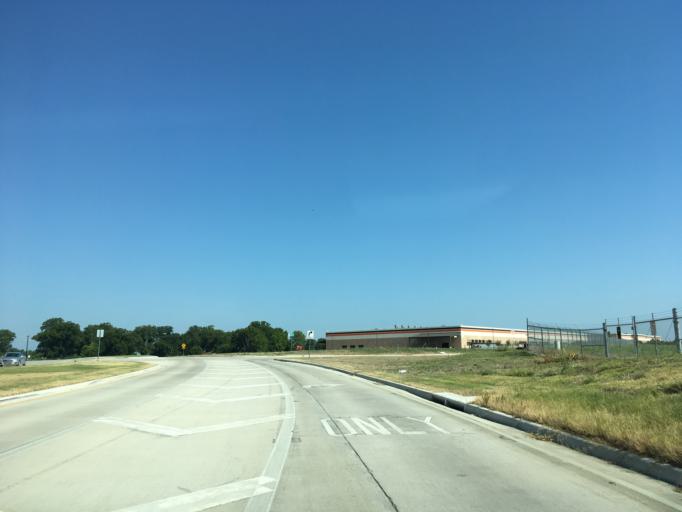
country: US
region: Texas
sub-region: Collin County
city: Fairview
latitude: 33.1648
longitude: -96.5955
